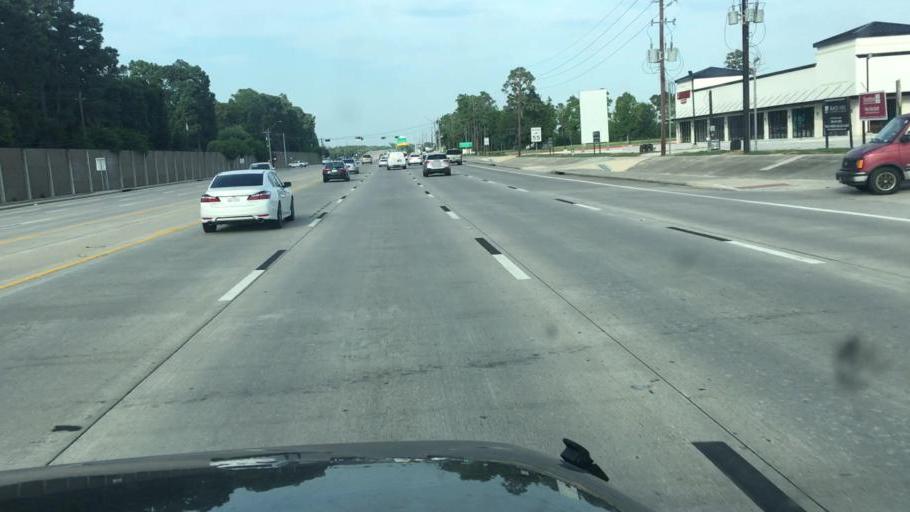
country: US
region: Texas
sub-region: Harris County
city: Spring
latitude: 30.0243
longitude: -95.4164
